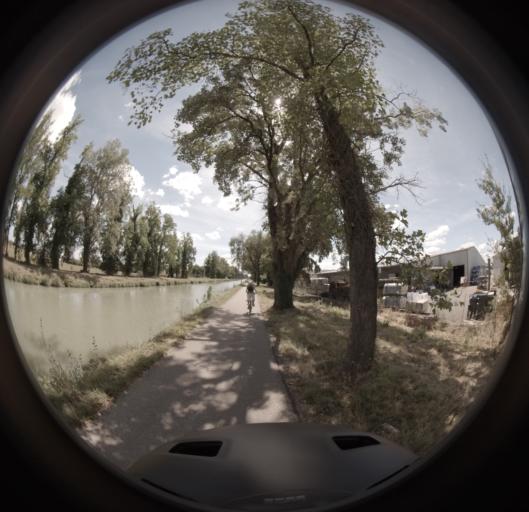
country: FR
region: Midi-Pyrenees
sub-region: Departement du Tarn-et-Garonne
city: Castelsarrasin
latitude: 44.0615
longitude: 1.1029
